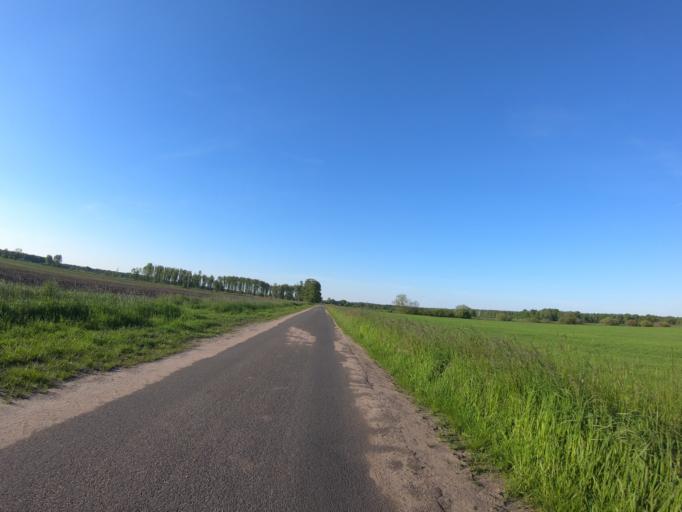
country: DE
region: Lower Saxony
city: Wagenhoff
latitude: 52.5339
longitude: 10.5637
